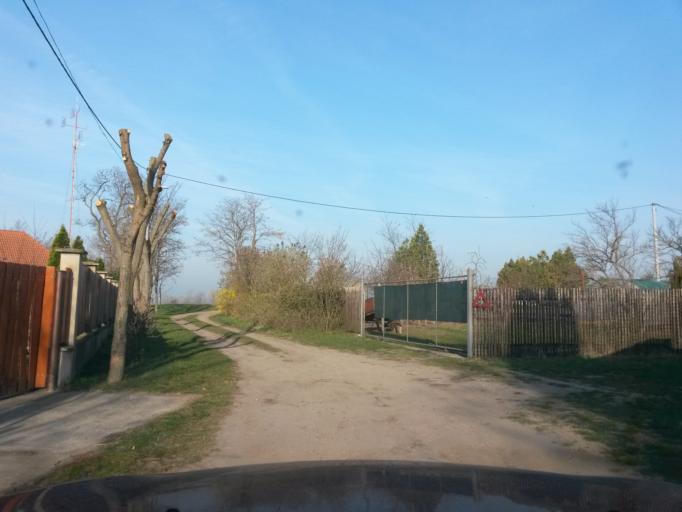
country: SK
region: Nitriansky
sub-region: Okres Komarno
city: Hurbanovo
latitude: 47.8835
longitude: 18.1724
